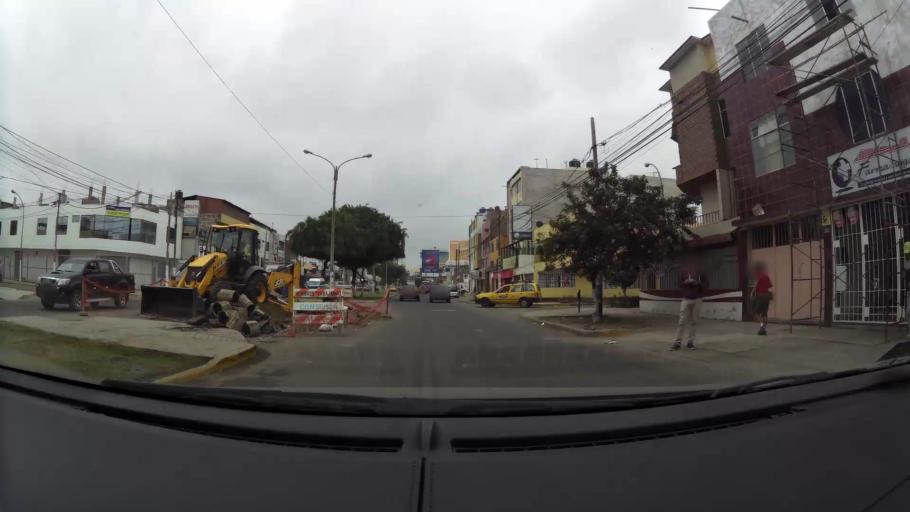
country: PE
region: La Libertad
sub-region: Provincia de Trujillo
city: Trujillo
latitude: -8.1206
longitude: -79.0200
